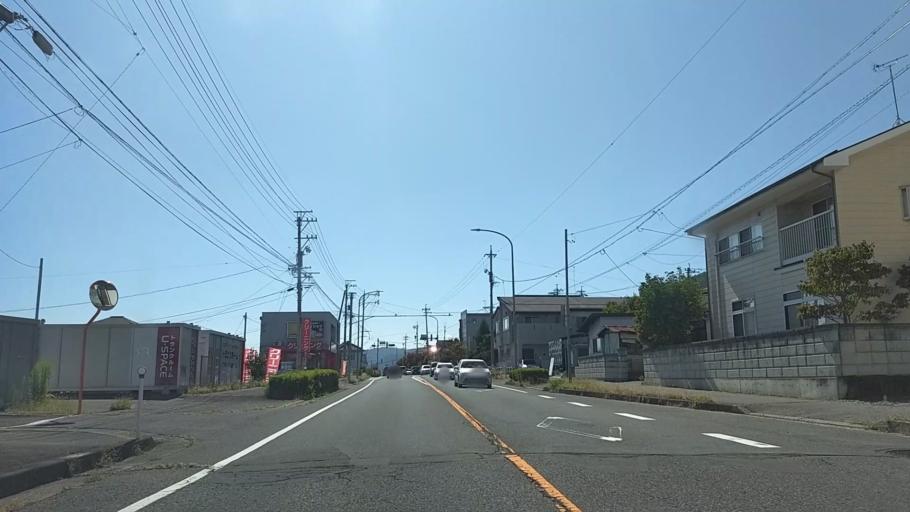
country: JP
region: Nagano
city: Nagano-shi
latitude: 36.6402
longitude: 138.1757
